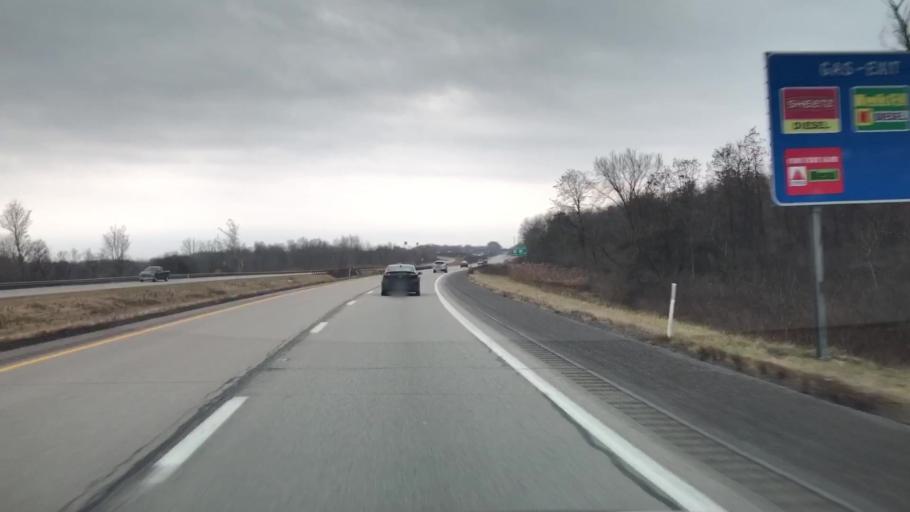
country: US
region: Pennsylvania
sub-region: Mercer County
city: Grove City
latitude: 41.1537
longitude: -80.1568
